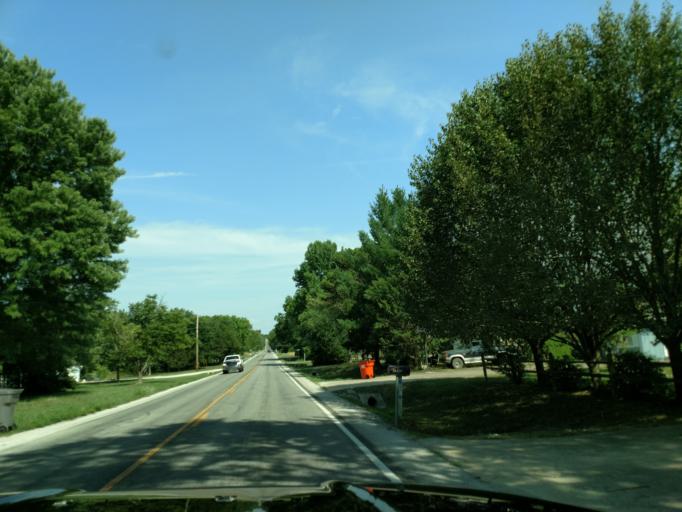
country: US
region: Missouri
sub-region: Barry County
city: Shell Knob
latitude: 36.6180
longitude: -93.6067
